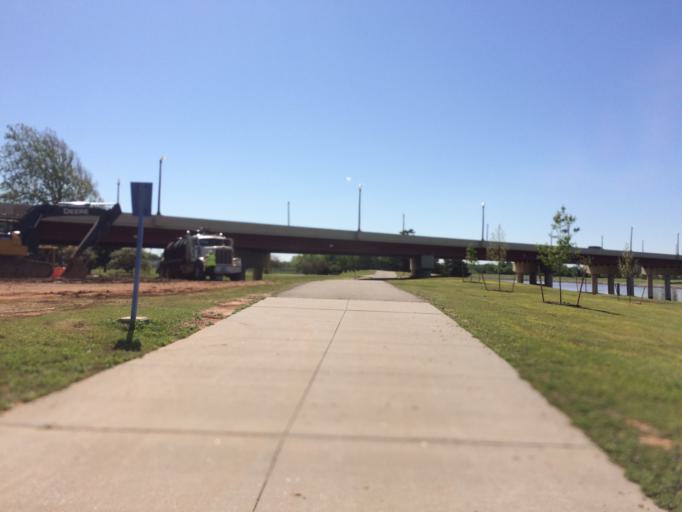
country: US
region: Oklahoma
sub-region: Oklahoma County
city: Oklahoma City
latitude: 35.4544
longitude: -97.5308
